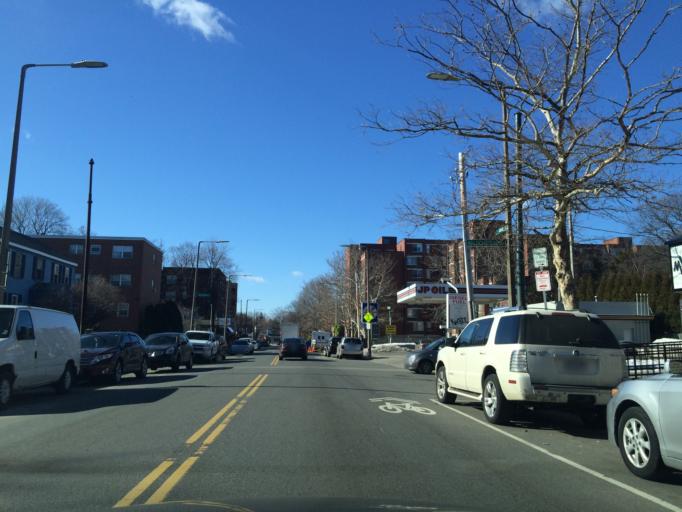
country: US
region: Massachusetts
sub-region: Suffolk County
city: Jamaica Plain
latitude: 42.3177
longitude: -71.1129
